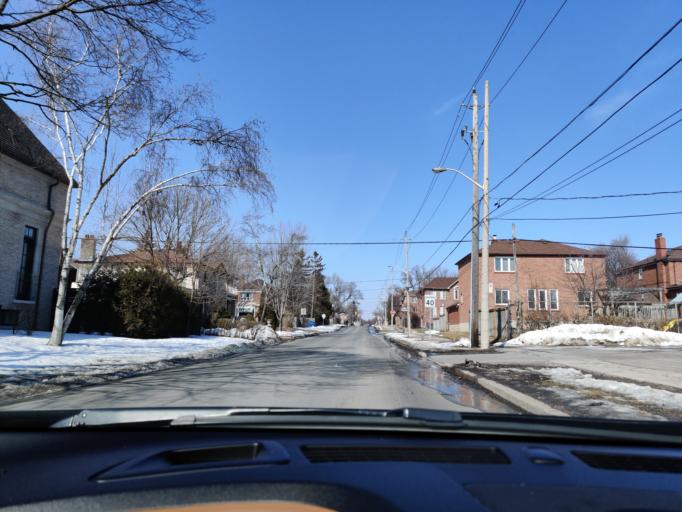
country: CA
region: Ontario
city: Toronto
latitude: 43.7164
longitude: -79.4321
